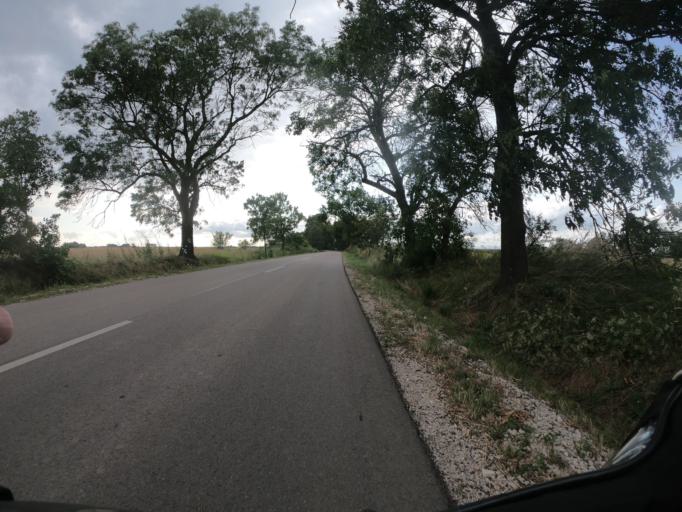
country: HU
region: Borsod-Abauj-Zemplen
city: Mezocsat
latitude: 47.8180
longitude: 20.8708
